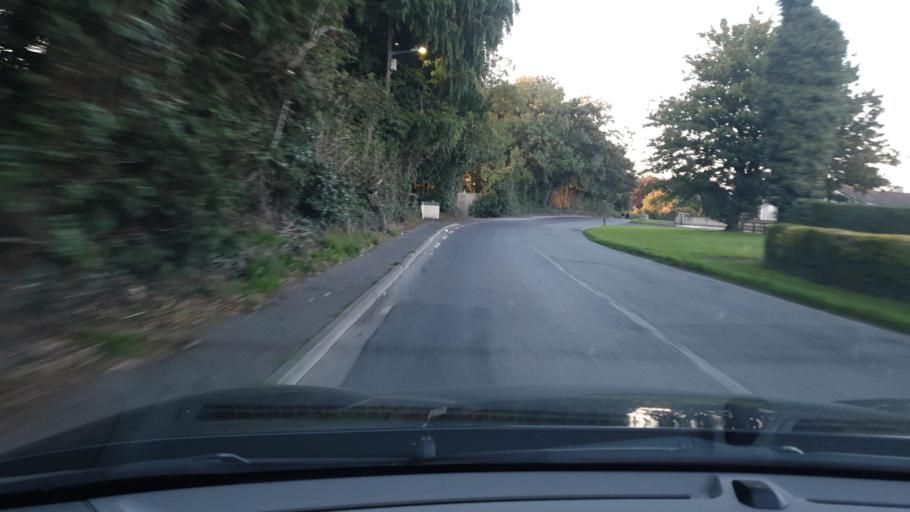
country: IE
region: Leinster
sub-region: Kildare
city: Prosperous
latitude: 53.3022
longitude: -6.8244
